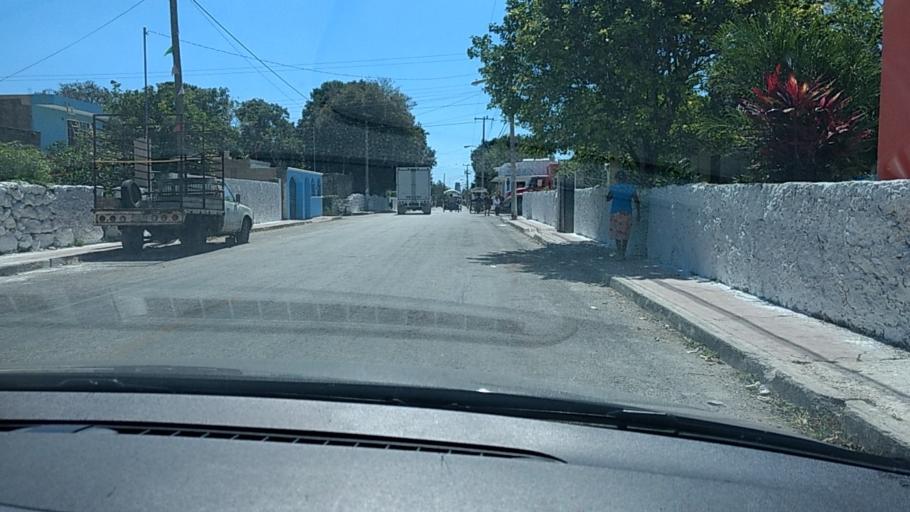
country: MX
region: Yucatan
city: Espita
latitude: 21.0204
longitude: -88.3050
